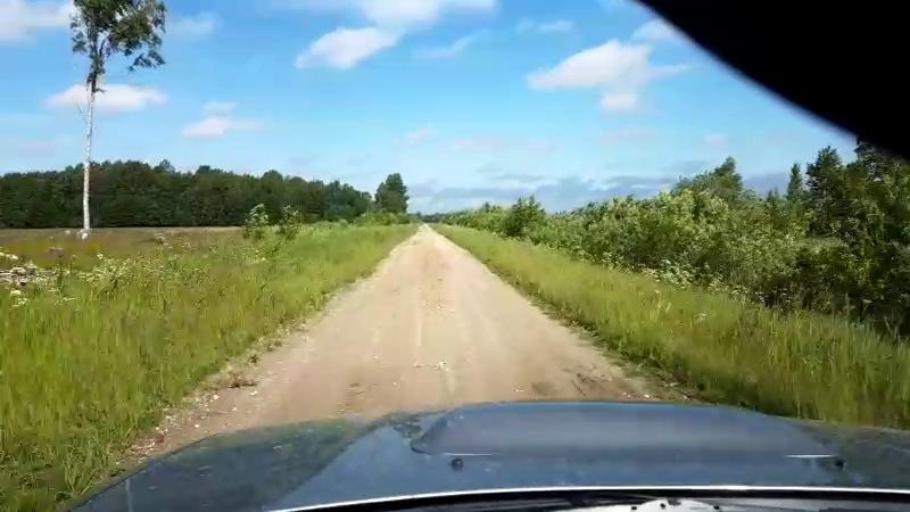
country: EE
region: Paernumaa
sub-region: Sindi linn
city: Sindi
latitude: 58.4890
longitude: 24.6575
